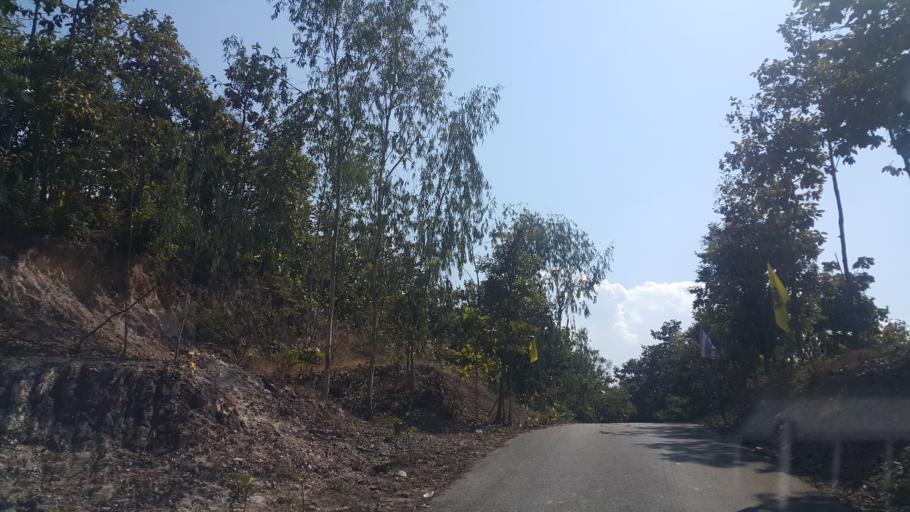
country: TH
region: Lamphun
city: Ban Thi
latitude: 18.6864
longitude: 99.1680
